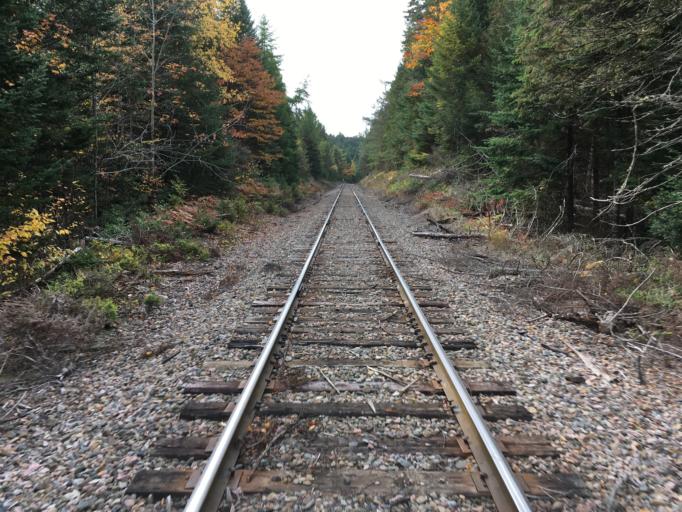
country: US
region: Vermont
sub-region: Caledonia County
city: Lyndonville
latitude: 44.6188
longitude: -71.9661
